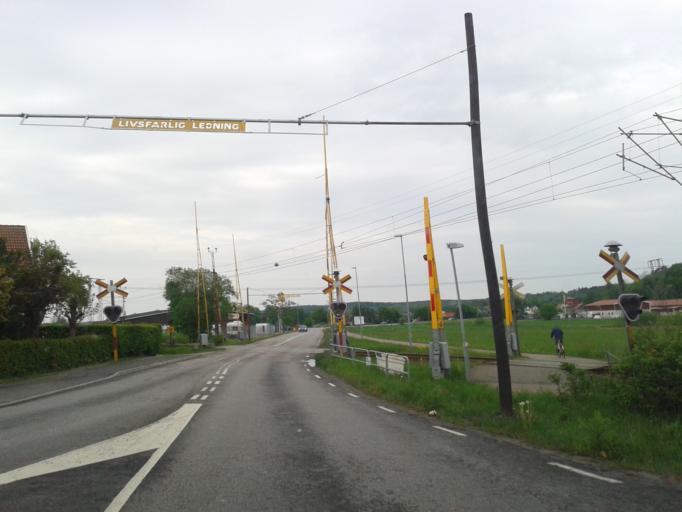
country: SE
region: Vaestra Goetaland
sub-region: Kungalvs Kommun
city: Kungalv
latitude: 57.8566
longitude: 11.9160
